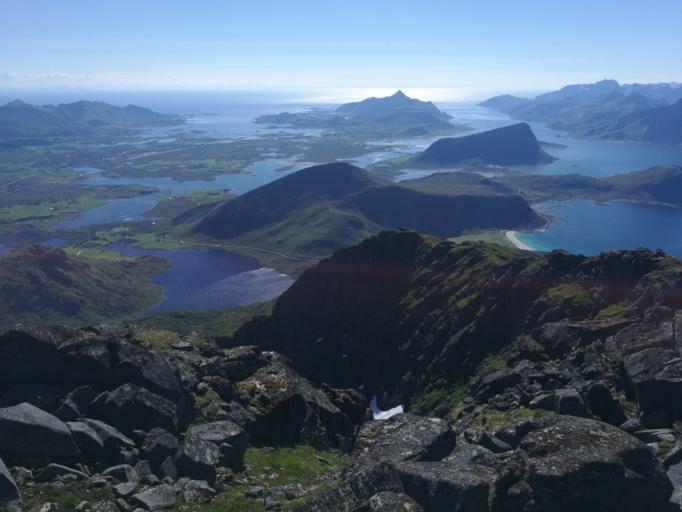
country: NO
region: Nordland
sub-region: Vestvagoy
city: Leknes
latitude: 68.2177
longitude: 13.5717
